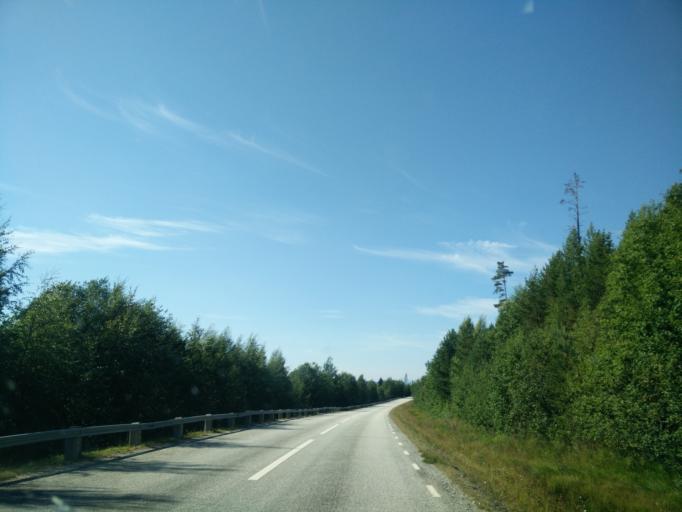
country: SE
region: Jaemtland
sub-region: Are Kommun
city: Jarpen
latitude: 62.8004
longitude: 13.5639
